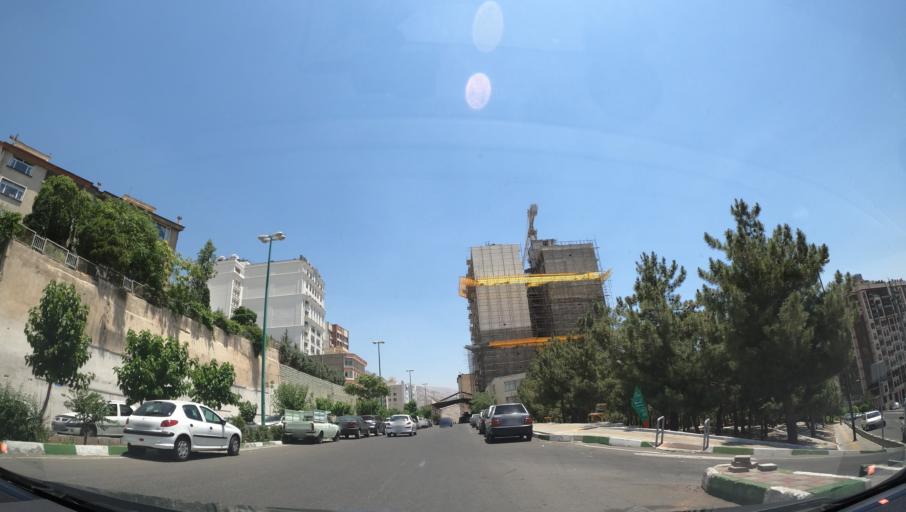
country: IR
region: Tehran
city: Tajrish
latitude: 35.8117
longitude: 51.3948
